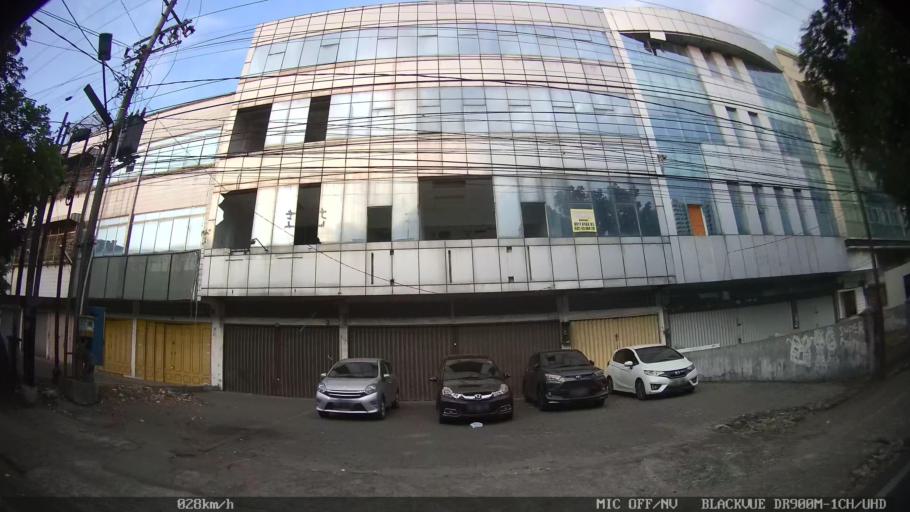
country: ID
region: North Sumatra
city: Medan
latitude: 3.5933
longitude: 98.6834
